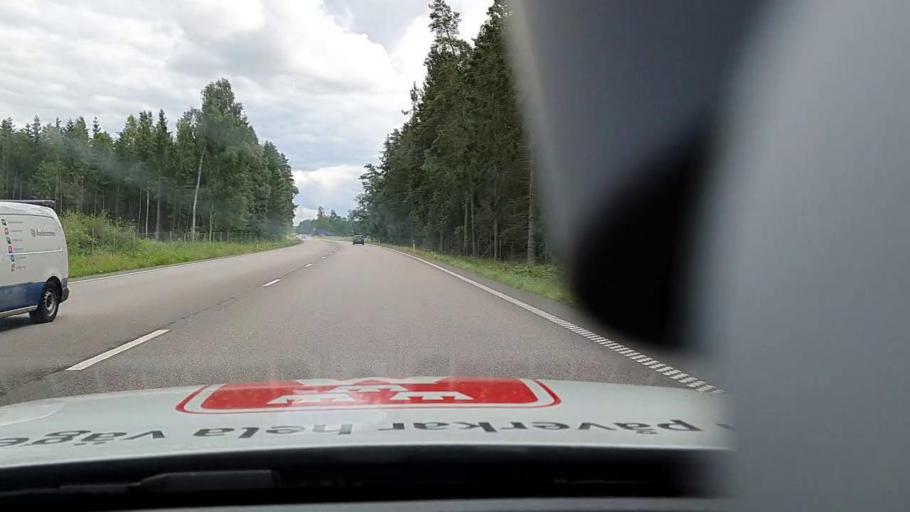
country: SE
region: Vaestra Goetaland
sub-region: Lidkopings Kommun
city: Vinninga
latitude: 58.4694
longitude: 13.2130
